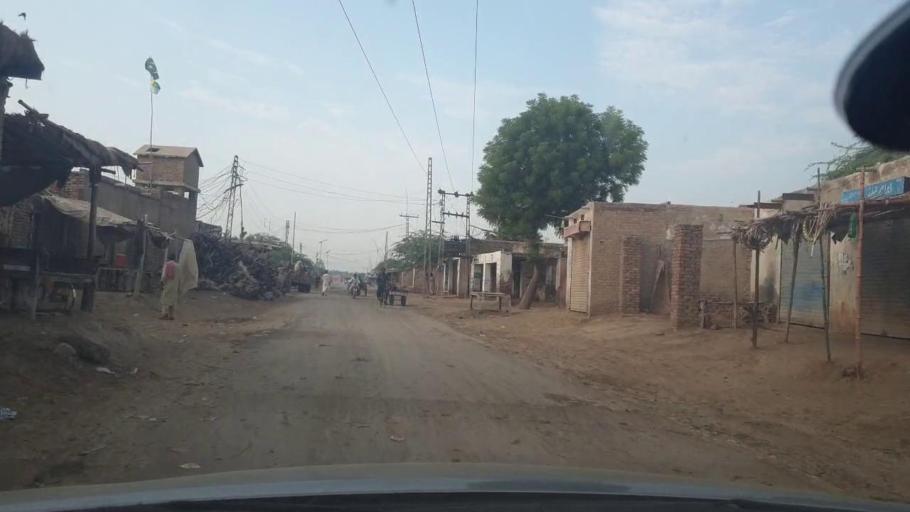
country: PK
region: Sindh
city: Jacobabad
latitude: 28.2679
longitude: 68.4195
